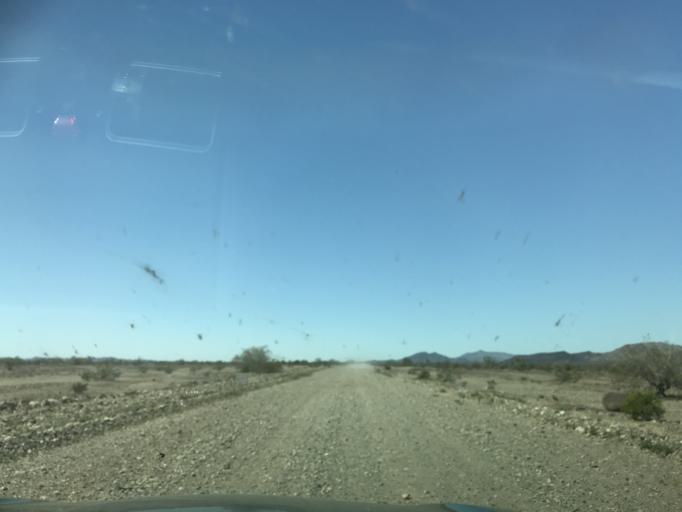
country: US
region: California
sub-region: Riverside County
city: Mesa Verde
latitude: 33.4777
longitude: -114.9392
